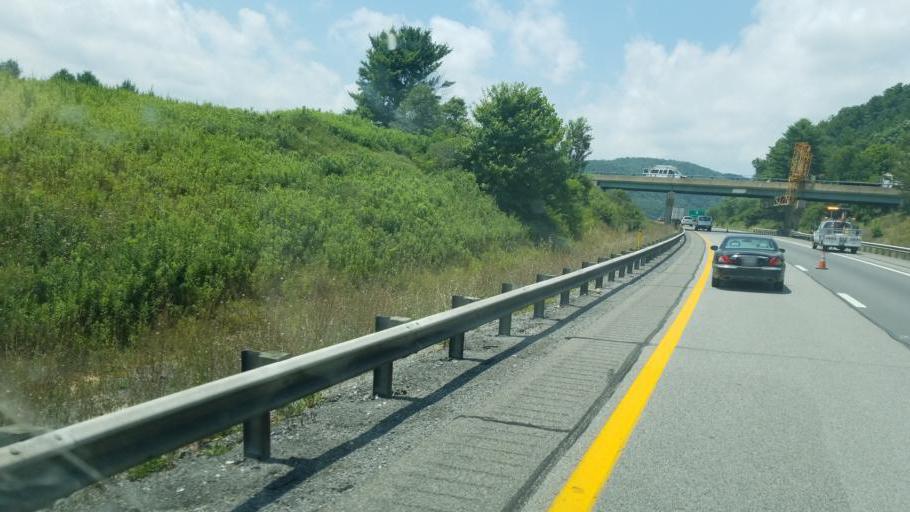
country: US
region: West Virginia
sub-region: Mercer County
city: Athens
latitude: 37.4933
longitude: -81.0930
